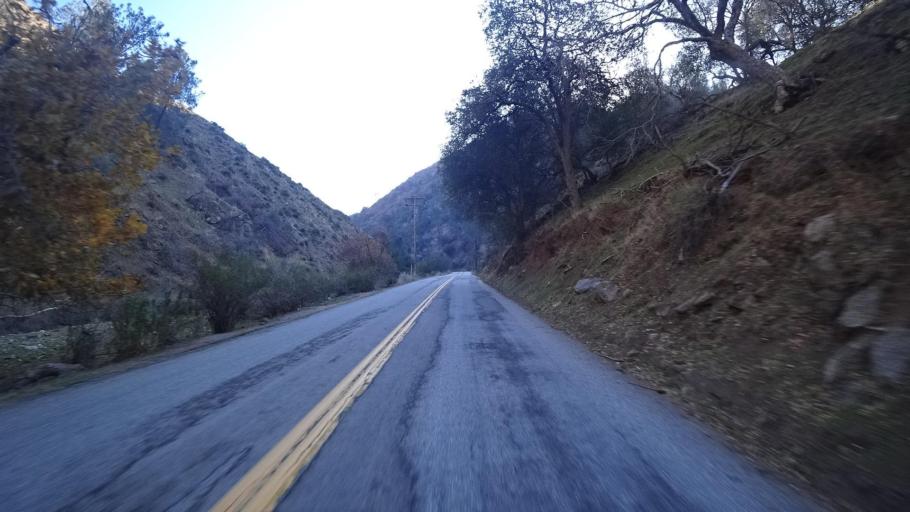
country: US
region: California
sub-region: Kern County
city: Golden Hills
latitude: 35.3151
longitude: -118.5233
